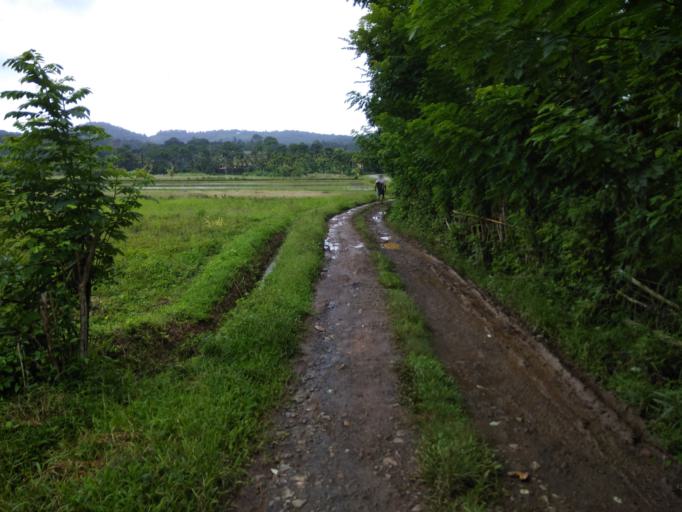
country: IN
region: Kerala
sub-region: Wayanad
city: Panamaram
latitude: 11.8514
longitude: 76.0440
